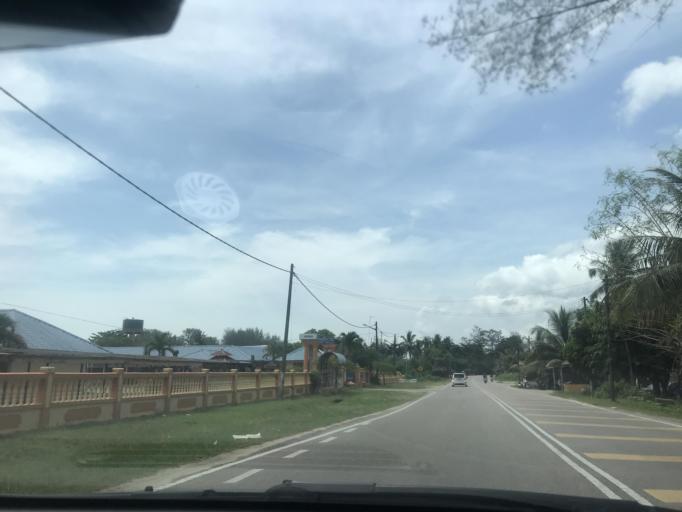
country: MY
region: Kelantan
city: Tumpat
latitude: 6.2172
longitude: 102.1219
